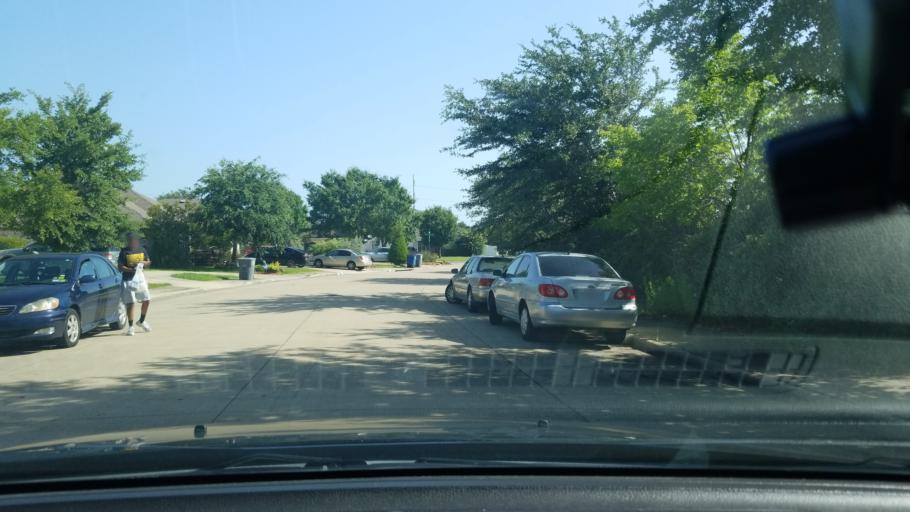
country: US
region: Texas
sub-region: Dallas County
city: Mesquite
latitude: 32.8050
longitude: -96.6746
